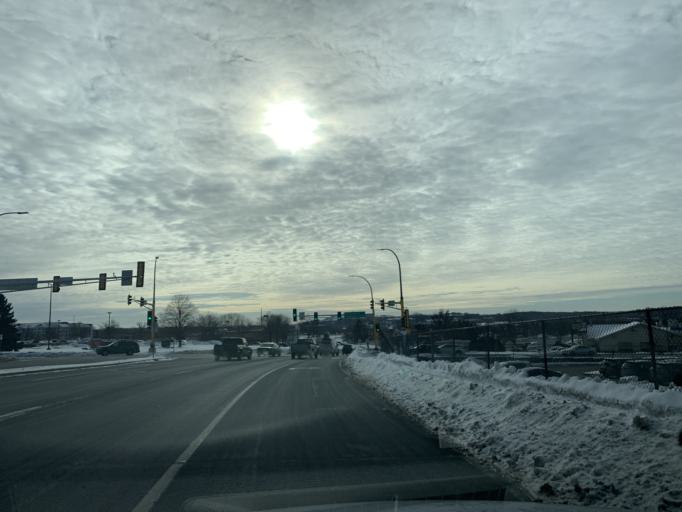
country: US
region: Minnesota
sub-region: Dakota County
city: Burnsville
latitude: 44.7471
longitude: -93.2780
